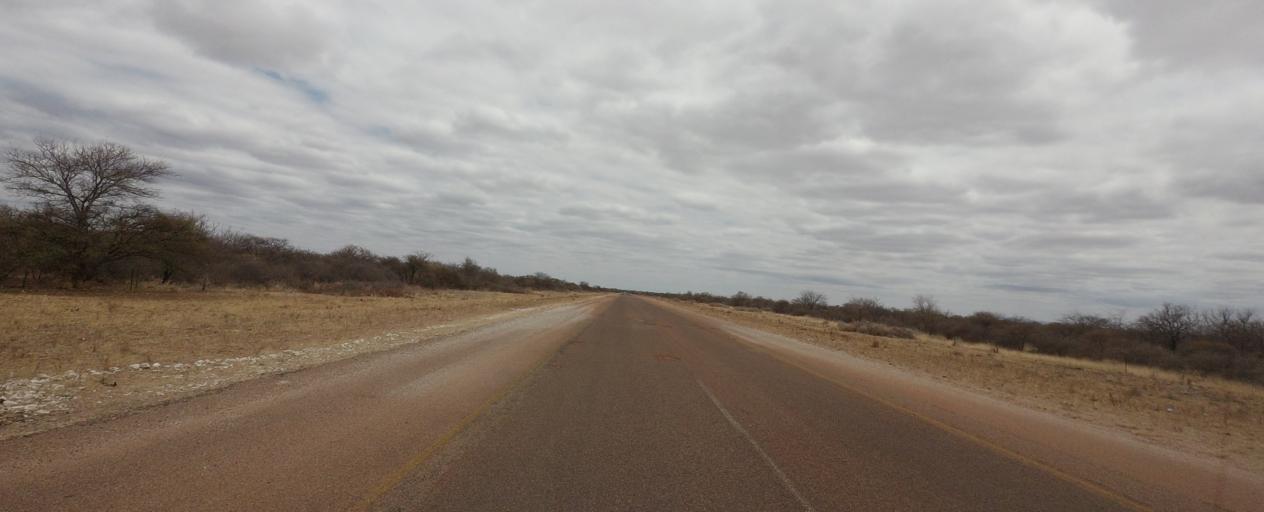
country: BW
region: Central
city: Makobeng
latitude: -22.8352
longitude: 28.2127
